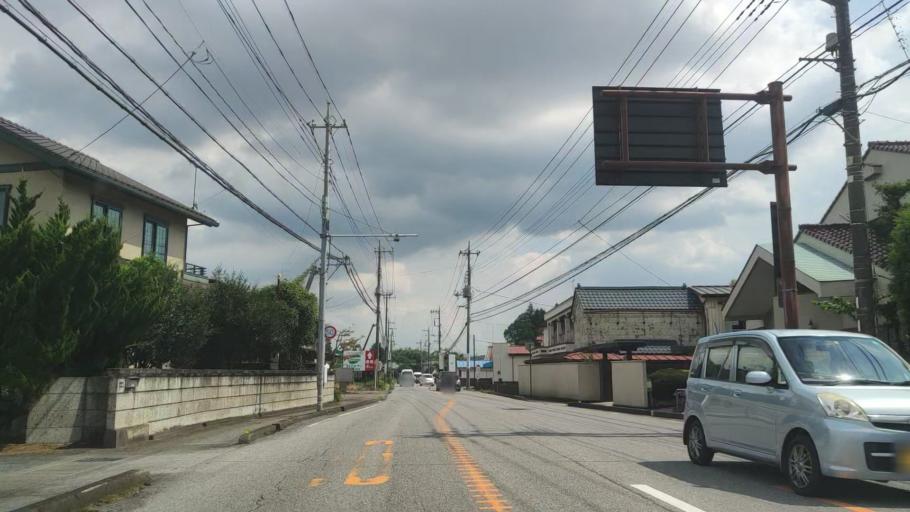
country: JP
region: Tochigi
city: Utsunomiya-shi
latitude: 36.6500
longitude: 139.8445
